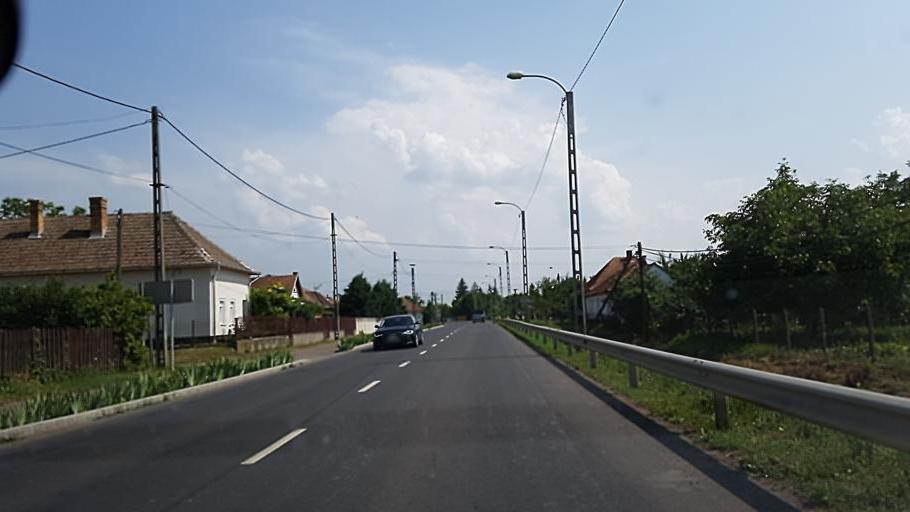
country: HU
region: Heves
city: Poroszlo
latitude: 47.6415
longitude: 20.6401
